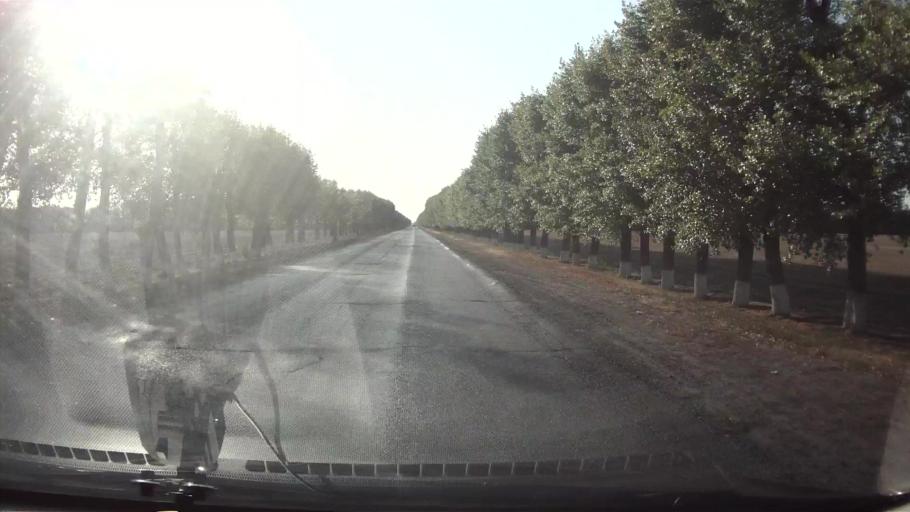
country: RU
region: Rostov
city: Tselina
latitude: 46.5272
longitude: 41.0677
